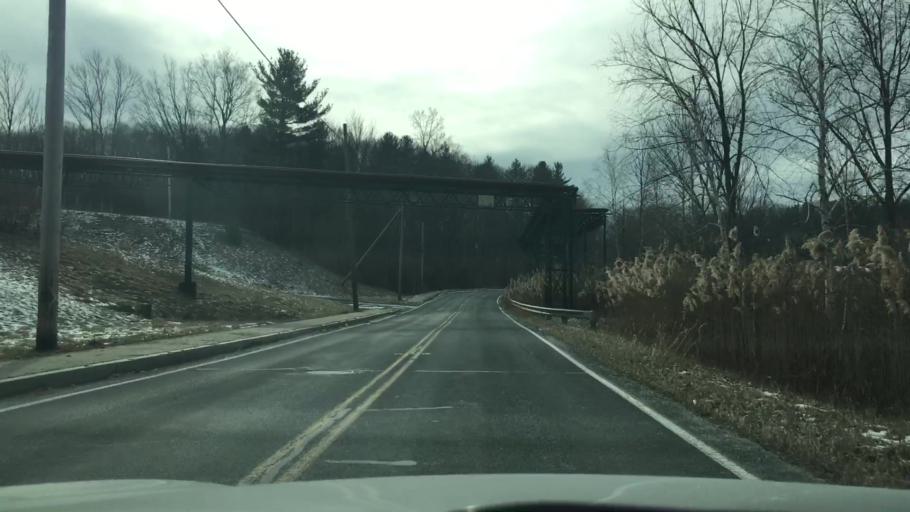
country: US
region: Massachusetts
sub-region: Berkshire County
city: Lee
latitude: 42.3183
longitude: -73.2438
